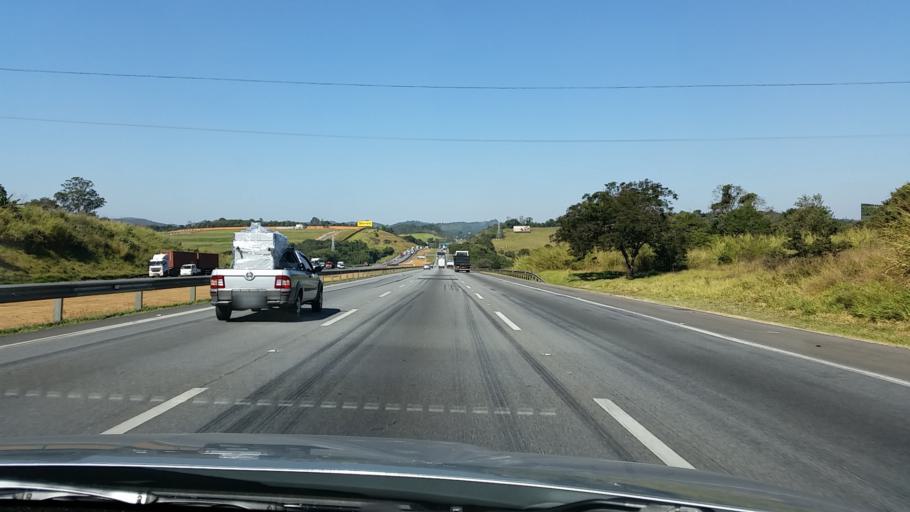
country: BR
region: Sao Paulo
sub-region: Jundiai
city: Jundiai
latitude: -23.2351
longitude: -46.8917
